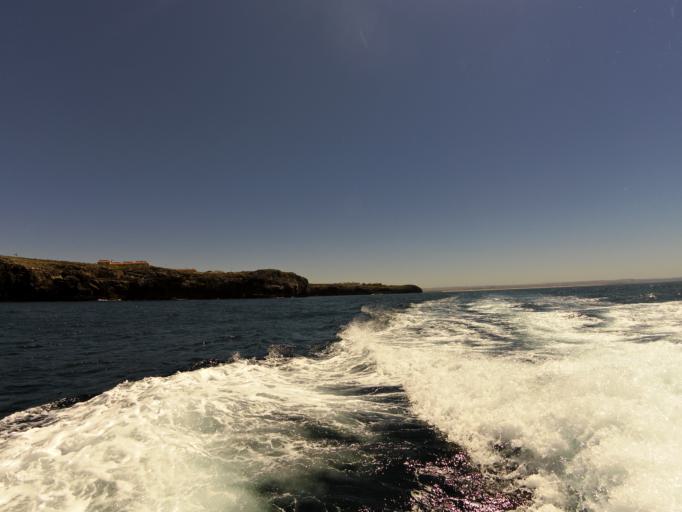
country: PT
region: Leiria
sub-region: Peniche
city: Peniche
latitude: 39.3555
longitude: -9.4049
